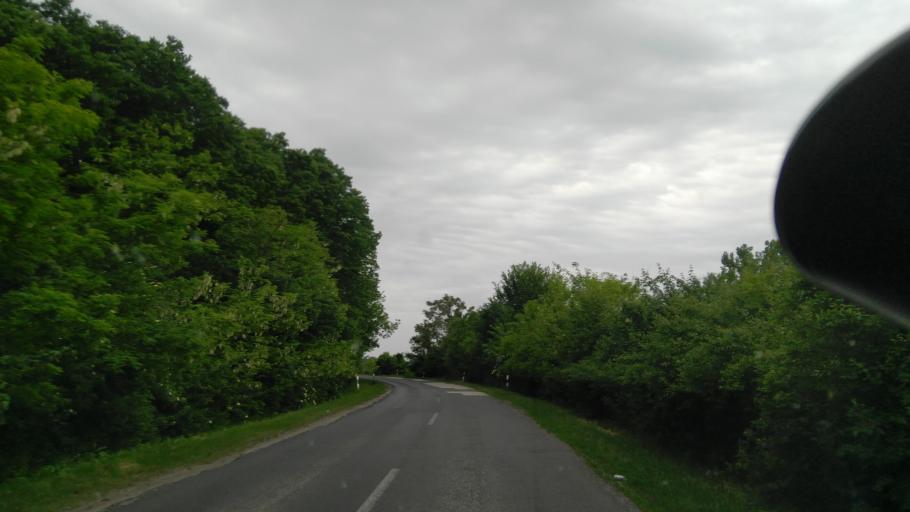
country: HU
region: Bekes
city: Doboz
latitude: 46.7322
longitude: 21.2647
